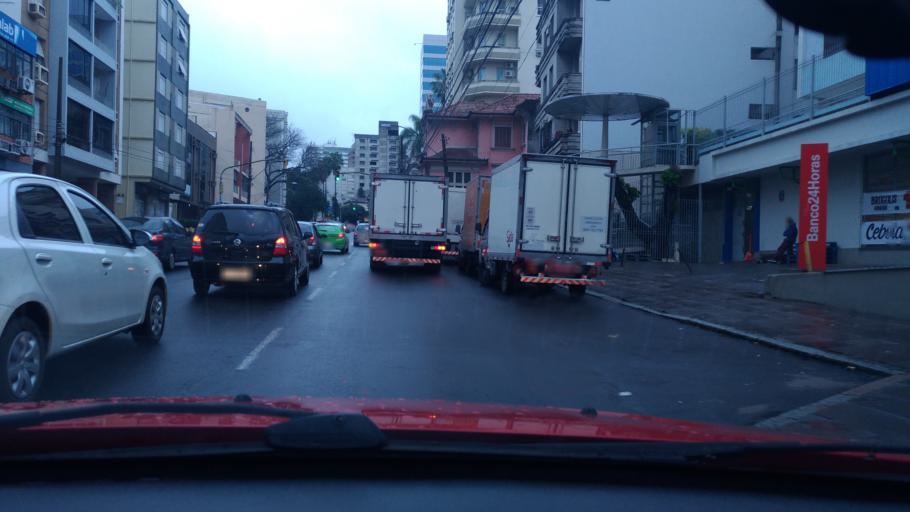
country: BR
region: Rio Grande do Sul
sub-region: Porto Alegre
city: Porto Alegre
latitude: -30.0294
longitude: -51.2136
